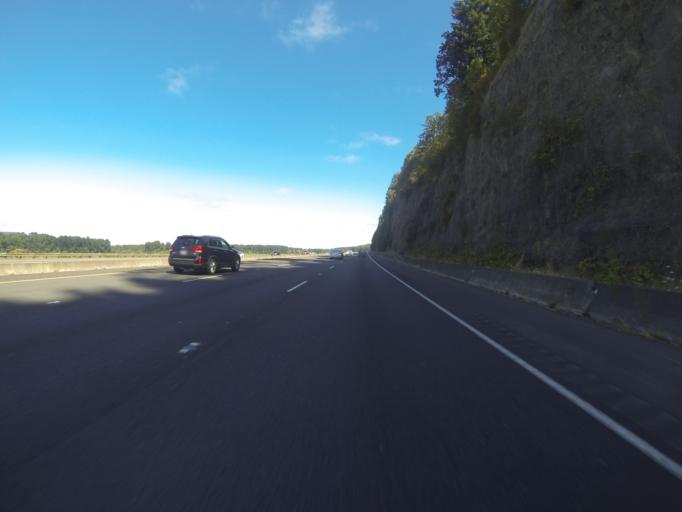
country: US
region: Washington
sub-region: Cowlitz County
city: Kalama
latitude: 46.0621
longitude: -122.8670
